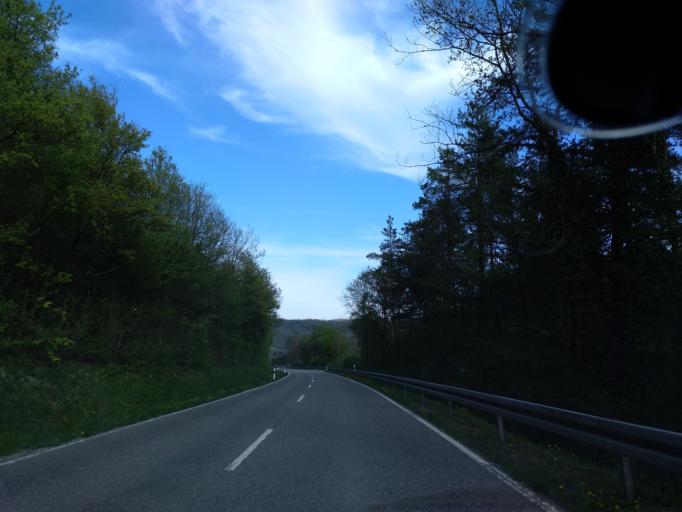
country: DE
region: Baden-Wuerttemberg
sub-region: Regierungsbezirk Stuttgart
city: Braunsbach
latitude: 49.2228
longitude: 9.7497
